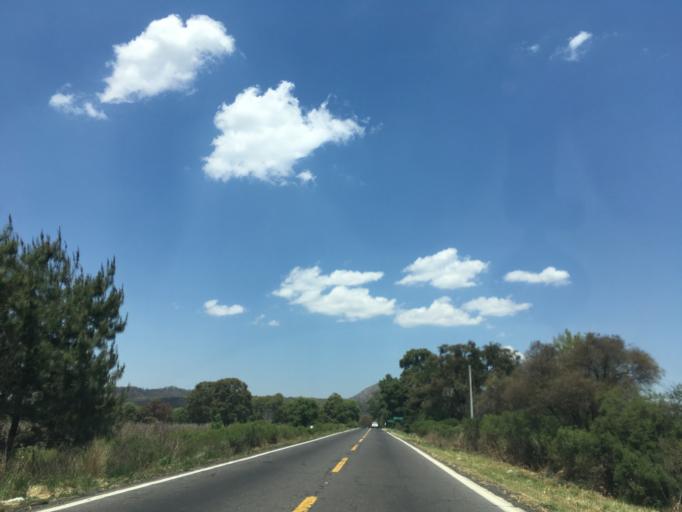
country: MX
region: Mexico
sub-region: Chalco
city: Zopoco
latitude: 19.7933
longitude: -102.0252
